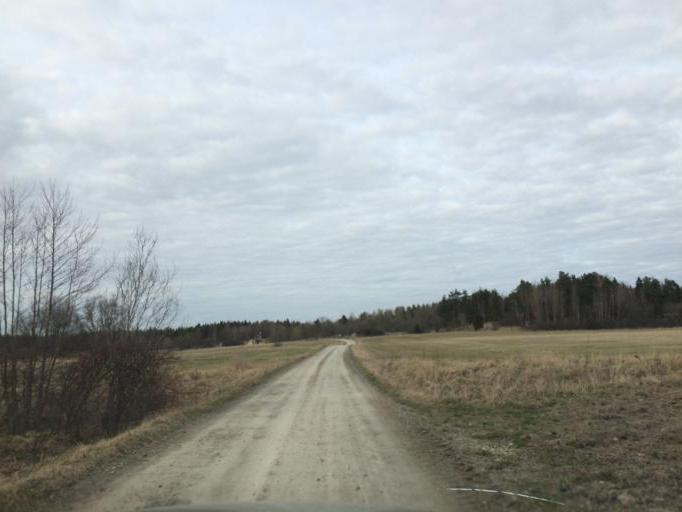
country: SE
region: Soedermanland
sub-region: Eskilstuna Kommun
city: Hallbybrunn
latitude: 59.4268
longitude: 16.3943
